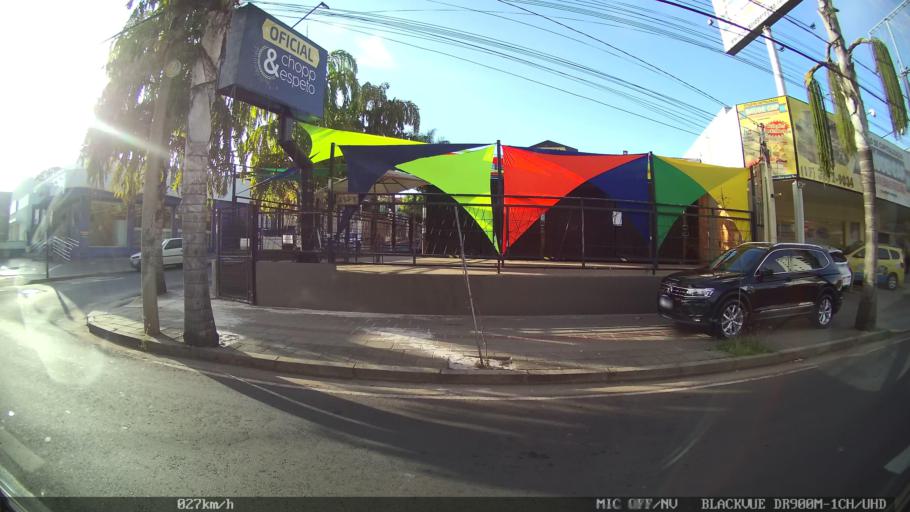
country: BR
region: Sao Paulo
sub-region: Sao Jose Do Rio Preto
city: Sao Jose do Rio Preto
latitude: -20.8188
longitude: -49.3823
